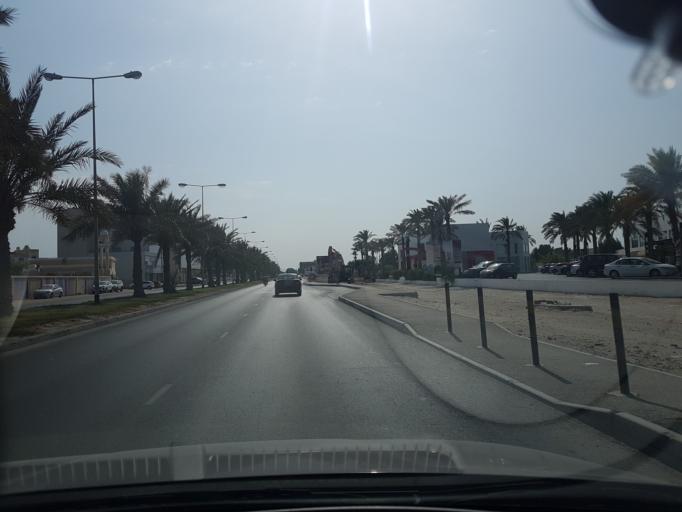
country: BH
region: Manama
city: Jidd Hafs
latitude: 26.2196
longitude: 50.4928
